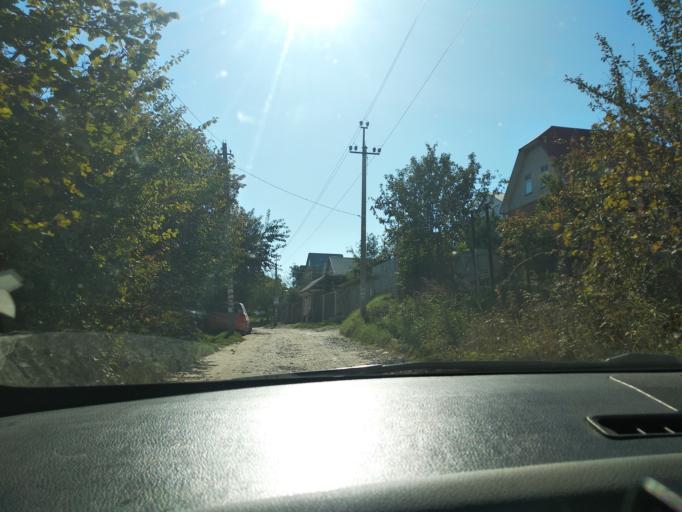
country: RU
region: Krasnodarskiy
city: Goryachiy Klyuch
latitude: 44.6213
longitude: 39.1605
